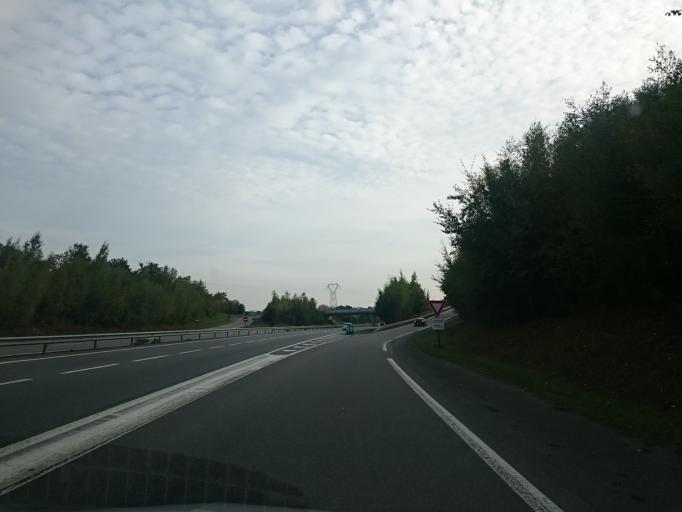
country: FR
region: Brittany
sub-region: Departement d'Ille-et-Vilaine
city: Saint-Armel
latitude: 48.0019
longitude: -1.5930
